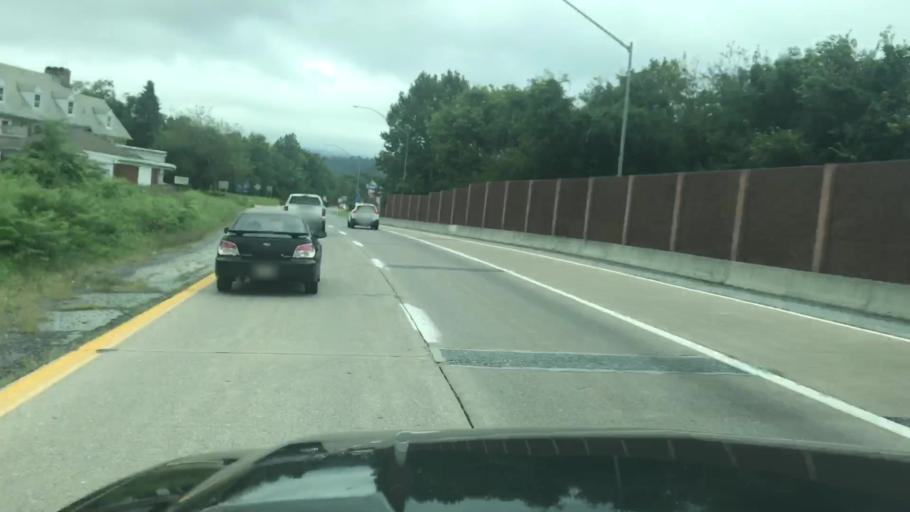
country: US
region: Pennsylvania
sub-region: Cumberland County
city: West Fairview
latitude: 40.3137
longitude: -76.8984
